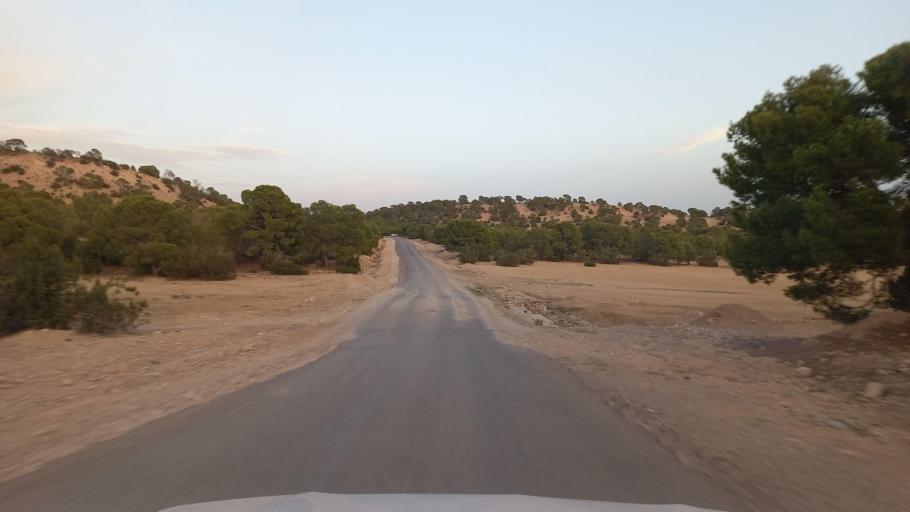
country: TN
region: Al Qasrayn
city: Sbiba
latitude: 35.4113
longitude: 8.9585
